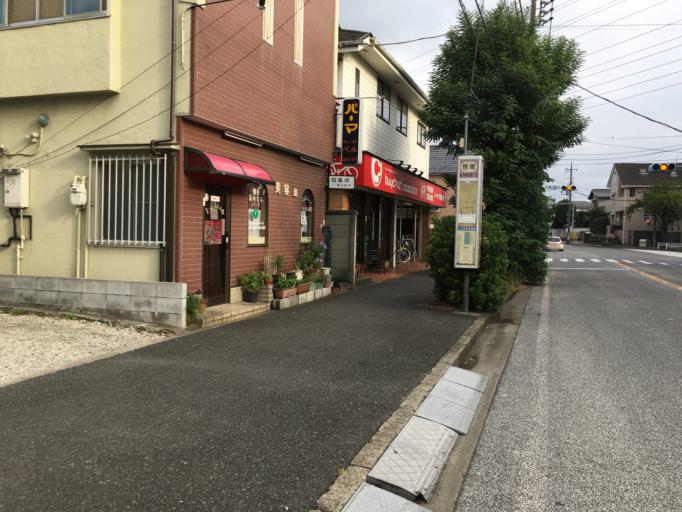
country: JP
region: Chiba
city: Kashiwa
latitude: 35.8142
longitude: 139.9506
